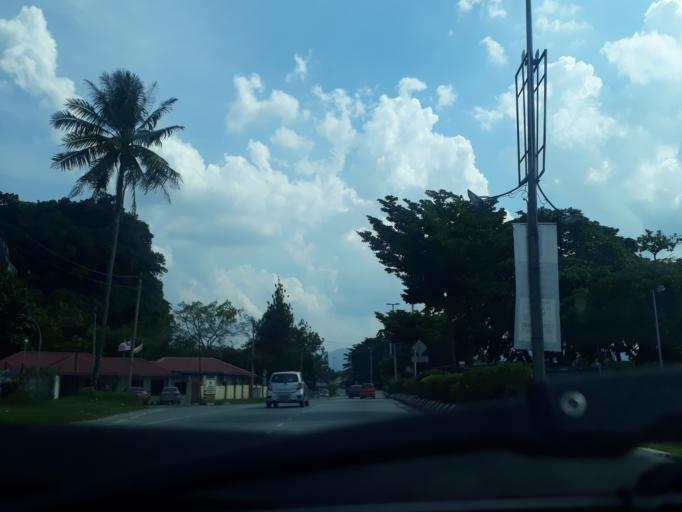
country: MY
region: Perak
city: Ipoh
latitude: 4.6456
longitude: 101.1000
